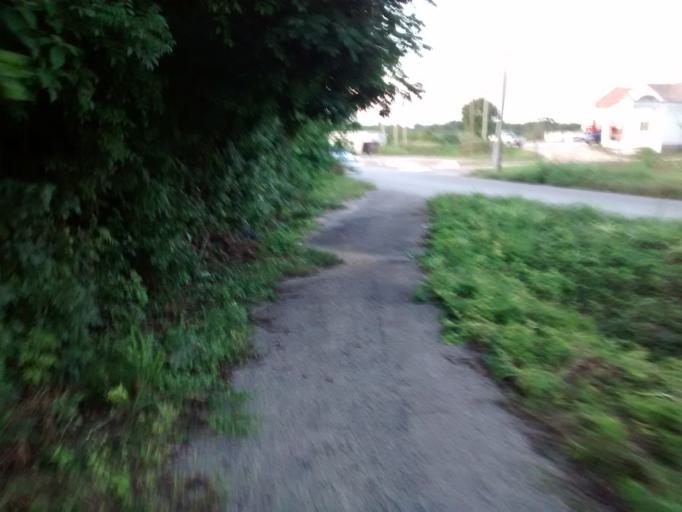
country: MX
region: Yucatan
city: Valladolid
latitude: 20.6956
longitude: -88.2299
